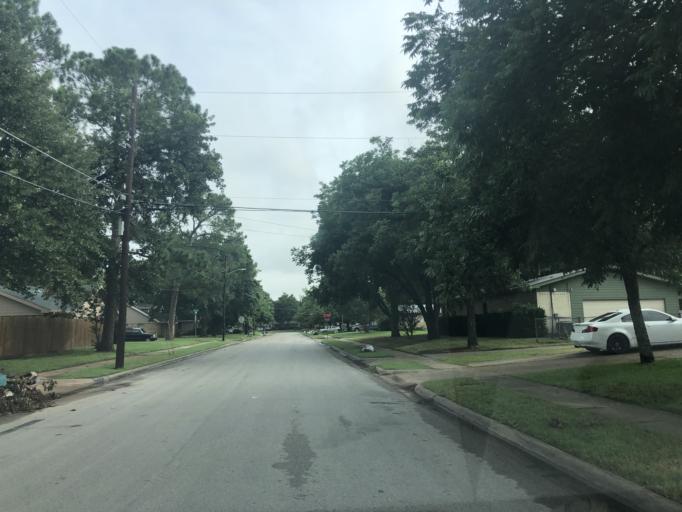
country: US
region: Texas
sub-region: Dallas County
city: Irving
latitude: 32.8028
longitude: -96.9831
